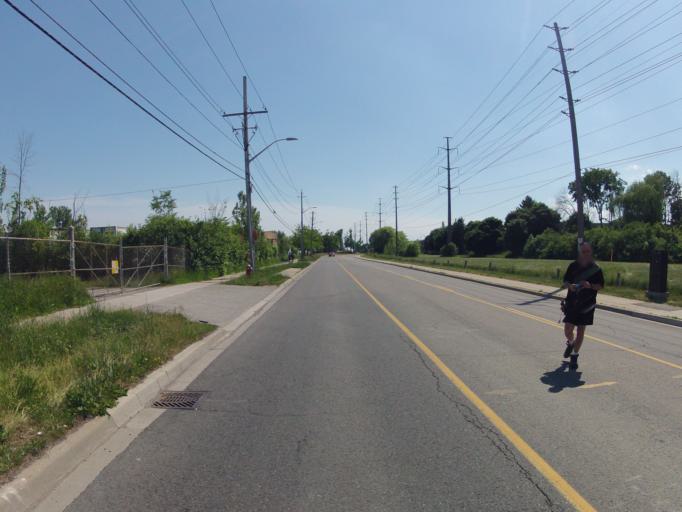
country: CA
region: Ontario
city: Mississauga
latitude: 43.5108
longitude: -79.6387
